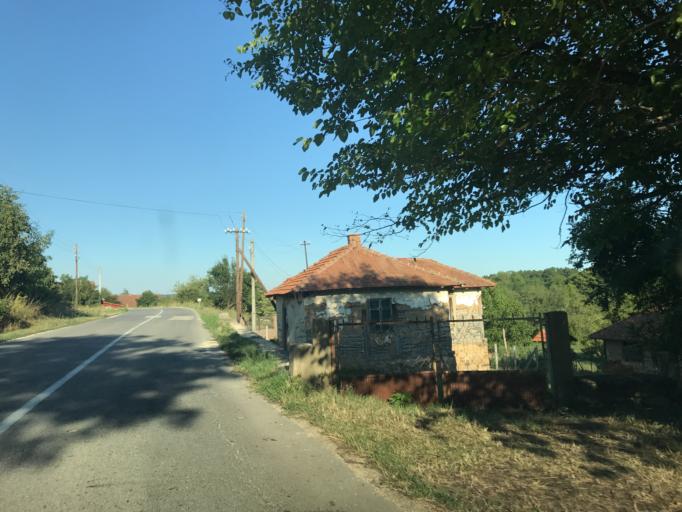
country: RO
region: Mehedinti
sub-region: Comuna Gogosu
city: Ostrovu Mare
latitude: 44.2919
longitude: 22.3411
